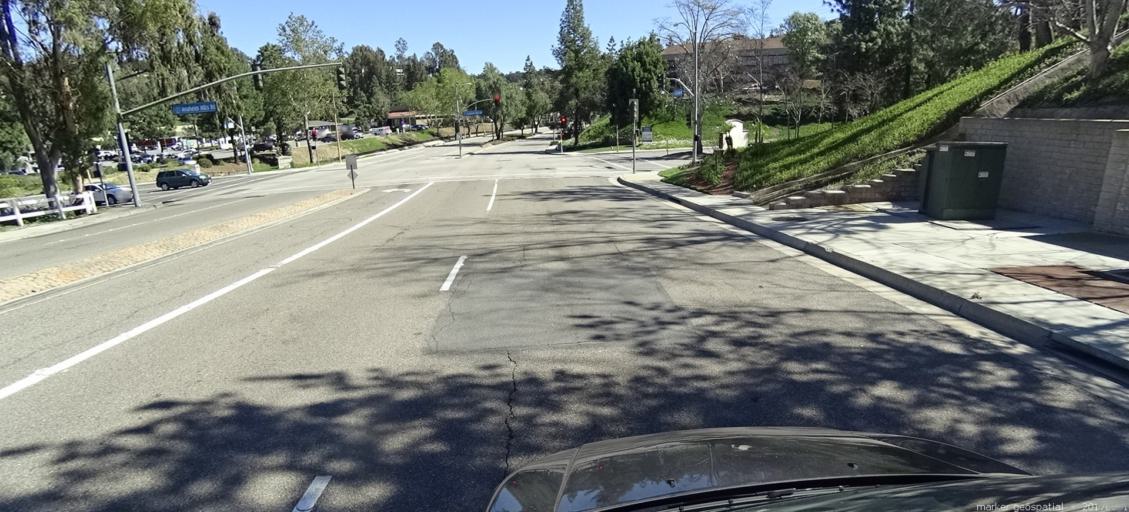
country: US
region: California
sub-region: Orange County
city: Villa Park
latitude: 33.8446
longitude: -117.7779
